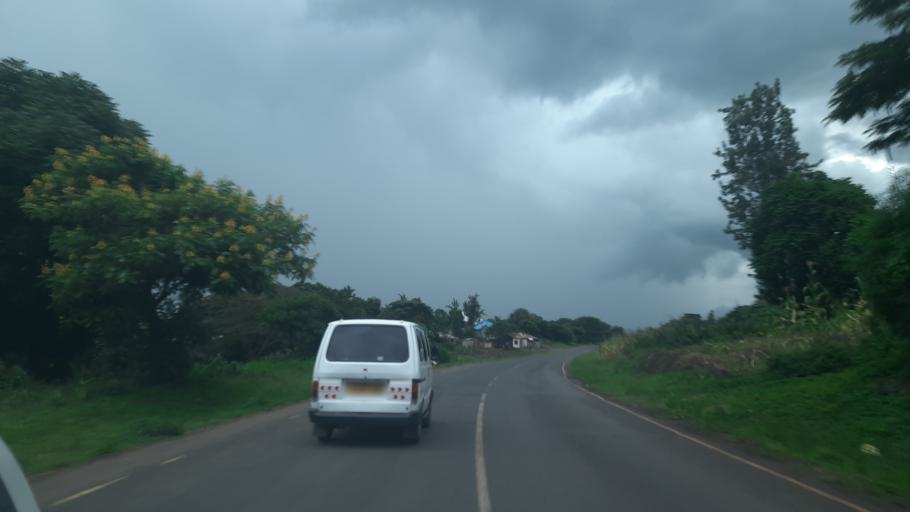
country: TZ
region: Arusha
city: Usa River
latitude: -3.3980
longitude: 36.8056
